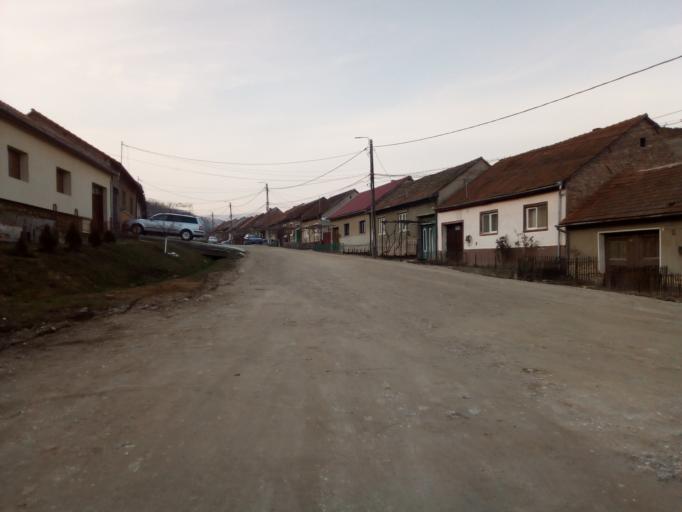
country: RO
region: Mehedinti
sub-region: Comuna Eselnita
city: Eselnita
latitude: 44.6944
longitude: 22.3635
